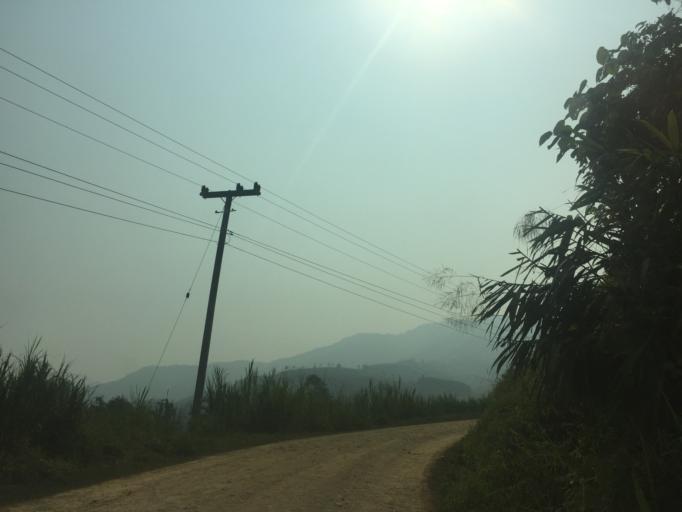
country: TH
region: Phayao
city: Phu Sang
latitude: 19.6733
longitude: 100.5206
